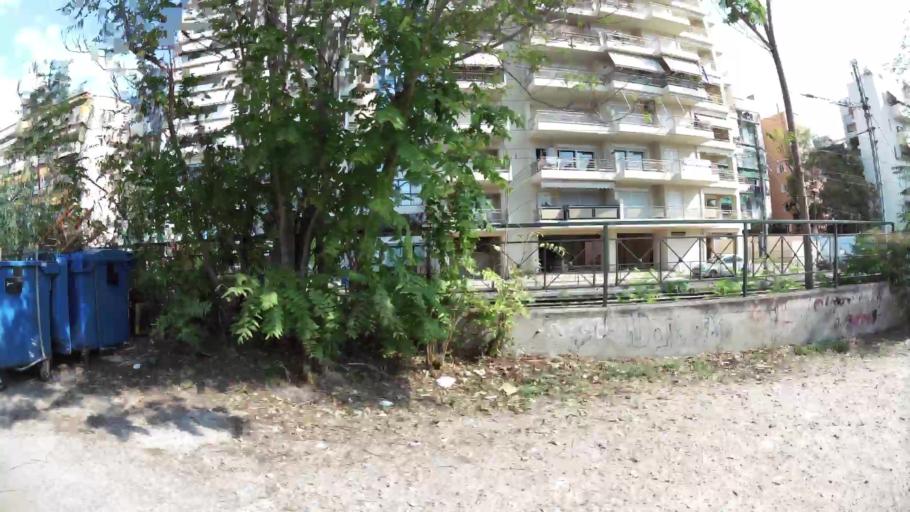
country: GR
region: Attica
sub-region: Nomarchia Athinas
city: Kipseli
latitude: 38.0081
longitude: 23.7212
